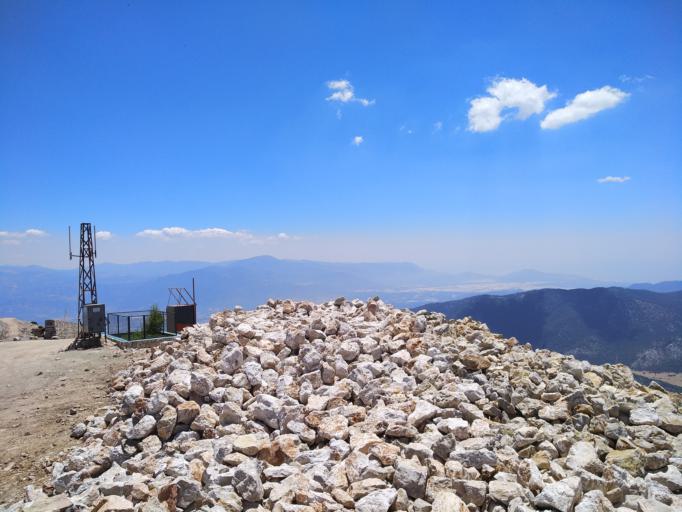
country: TR
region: Mugla
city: OEluedeniz
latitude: 36.5302
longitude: 29.1806
